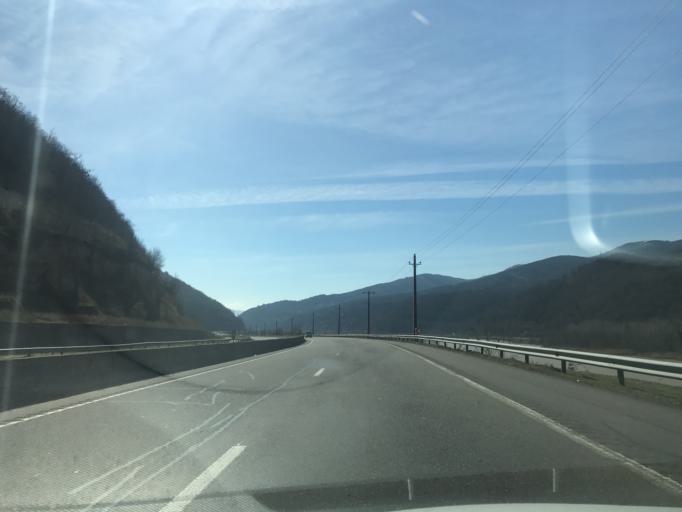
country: IR
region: Gilan
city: Pa'in-e Bazar-e Rudbar
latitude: 36.9812
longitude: 49.5634
